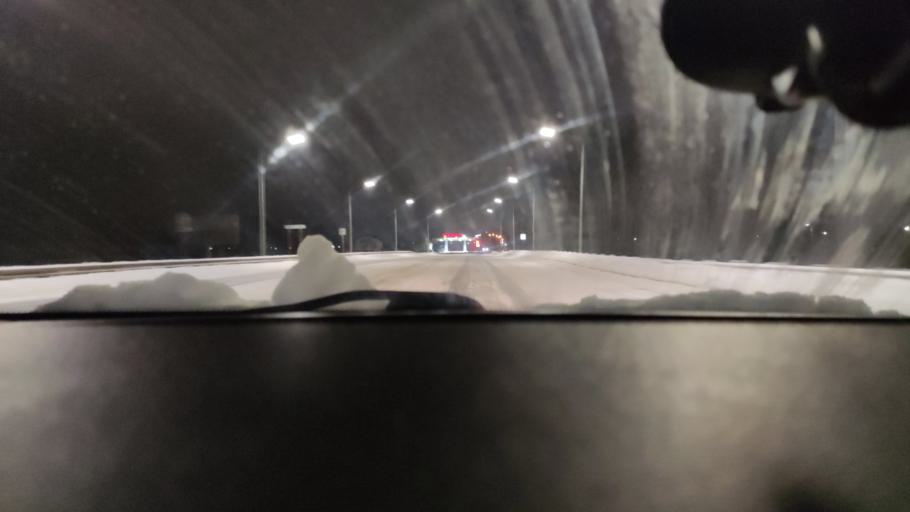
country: RU
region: Perm
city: Overyata
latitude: 58.0594
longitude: 55.8285
